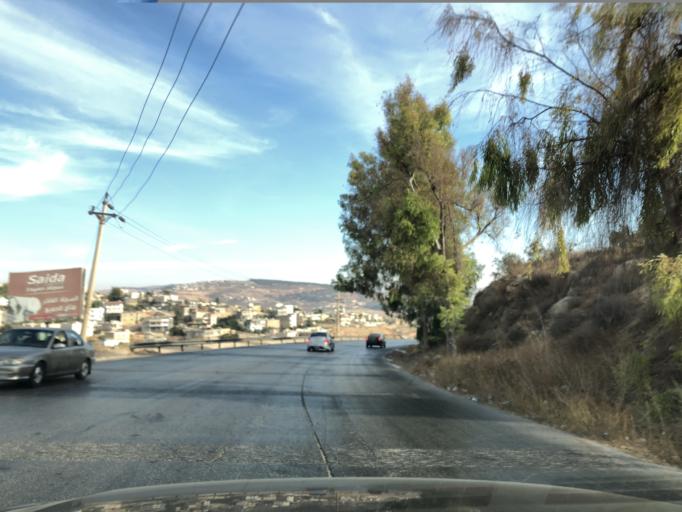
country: JO
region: Jerash
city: Jarash
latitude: 32.2778
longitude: 35.8783
